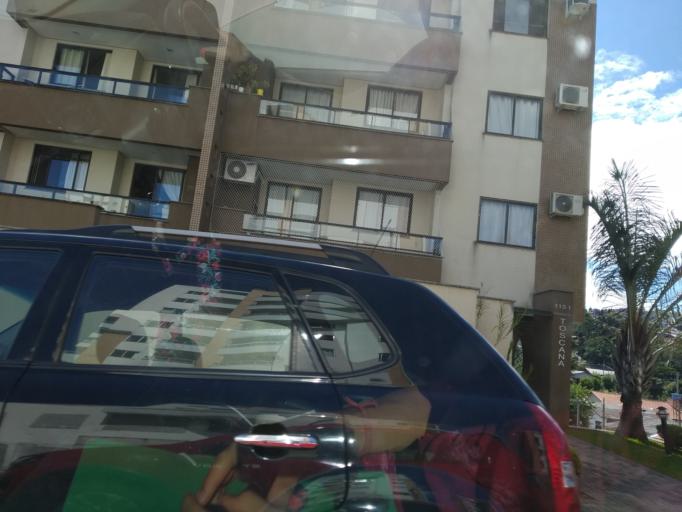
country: BR
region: Parana
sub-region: Pato Branco
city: Pato Branco
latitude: -26.2262
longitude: -52.6660
